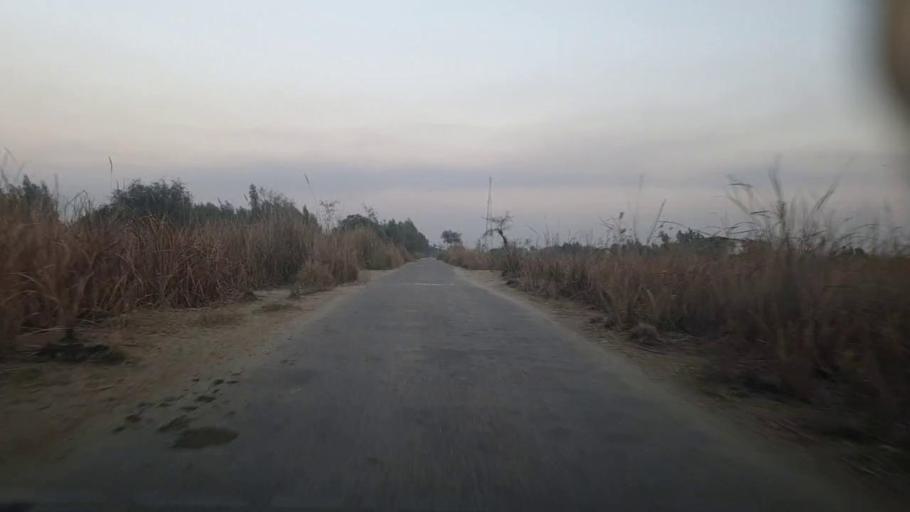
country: PK
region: Sindh
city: Kandiari
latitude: 26.6854
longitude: 68.9319
